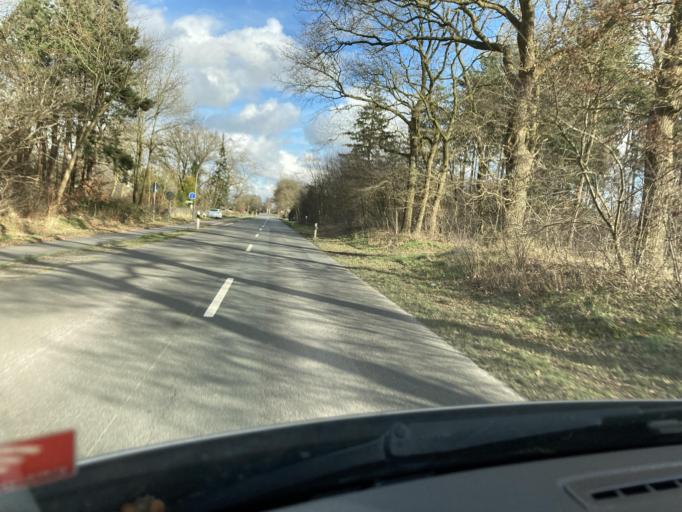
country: DE
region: Lower Saxony
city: Zetel
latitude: 53.4290
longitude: 7.9152
